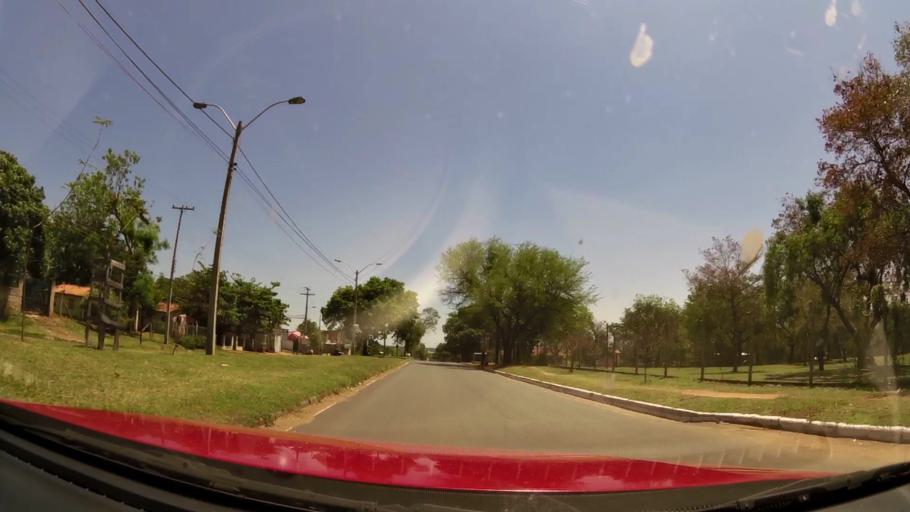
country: PY
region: Central
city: Colonia Mariano Roque Alonso
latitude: -25.2315
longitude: -57.5526
